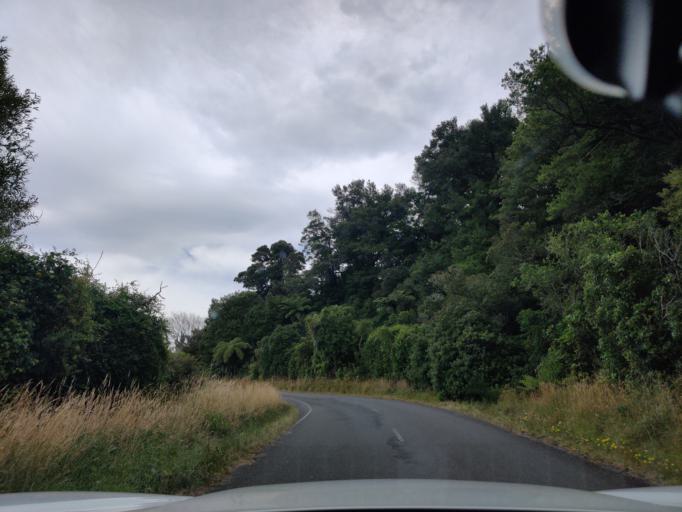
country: NZ
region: Wellington
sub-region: Masterton District
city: Masterton
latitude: -41.0368
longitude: 175.4212
